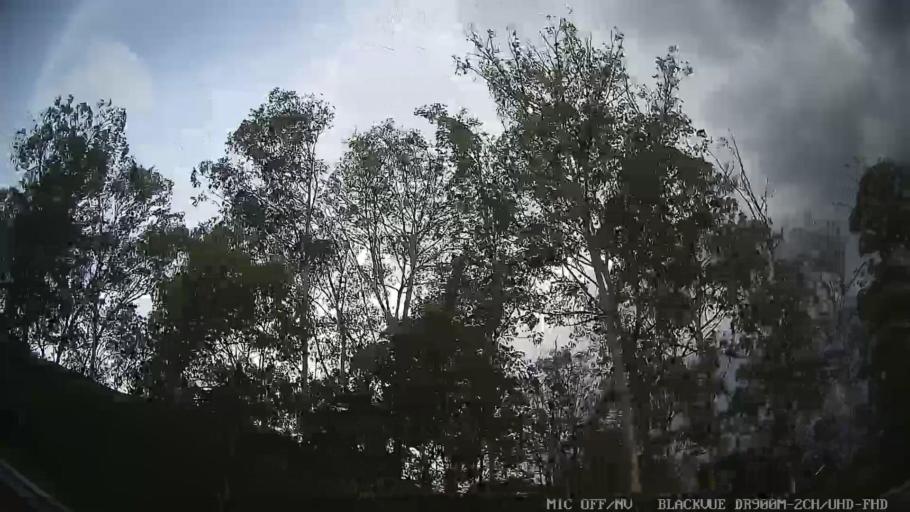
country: BR
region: Sao Paulo
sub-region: Itatiba
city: Itatiba
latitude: -22.9491
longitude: -46.8166
